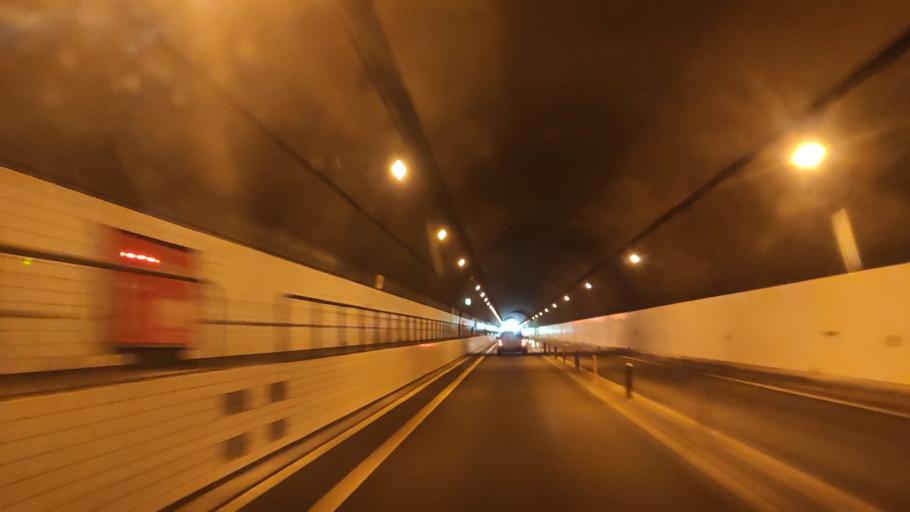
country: JP
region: Tokushima
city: Ikedacho
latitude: 34.0182
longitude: 133.7588
